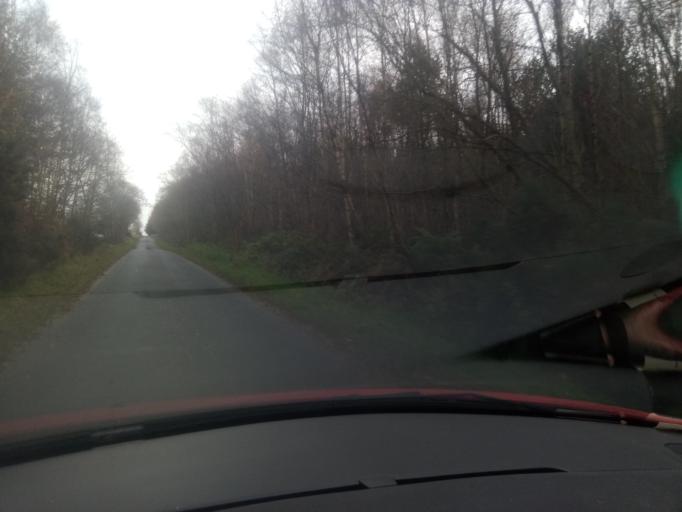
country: GB
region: Scotland
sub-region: The Scottish Borders
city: Jedburgh
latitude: 55.4848
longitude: -2.5893
